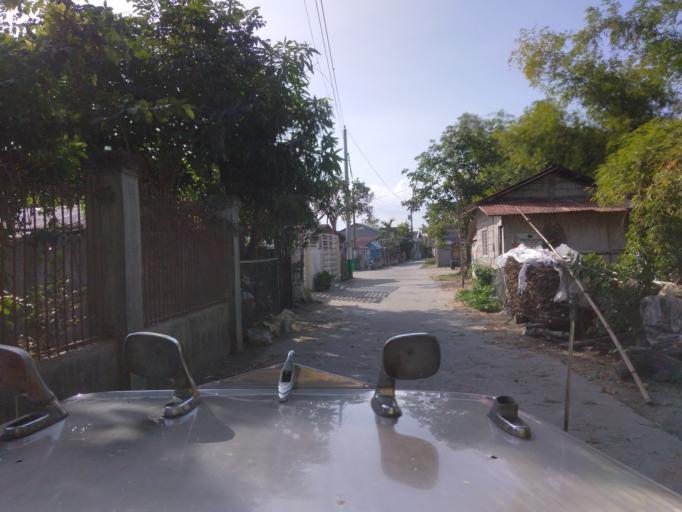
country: PH
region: Central Luzon
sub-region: Province of Pampanga
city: Malino
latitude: 15.1007
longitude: 120.6920
